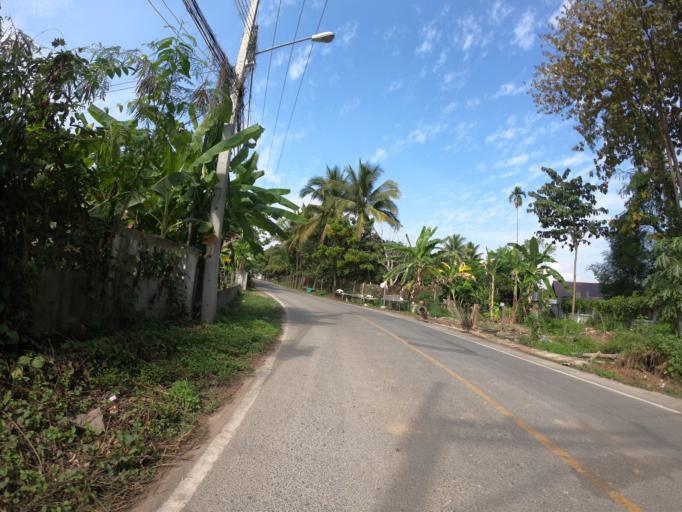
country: TH
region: Chiang Mai
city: San Sai
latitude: 18.8606
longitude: 99.0616
